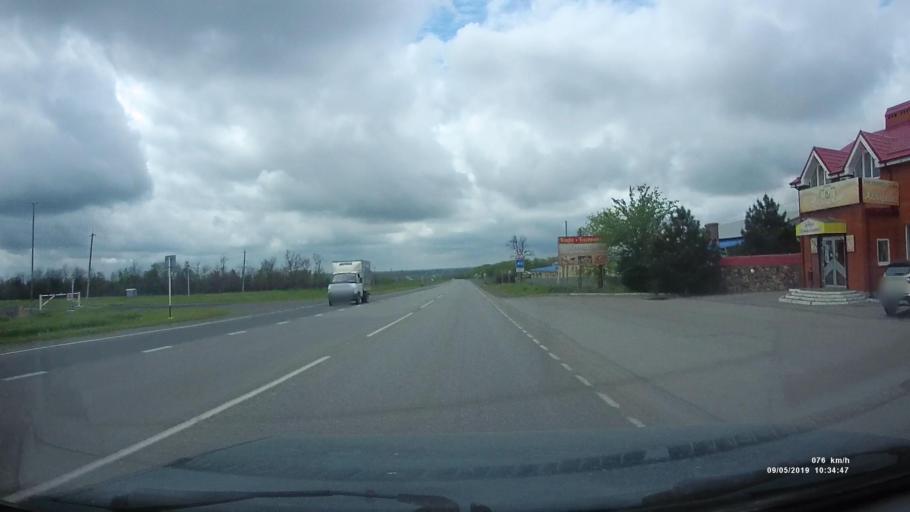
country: RU
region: Rostov
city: Peshkovo
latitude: 47.0501
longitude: 39.4170
